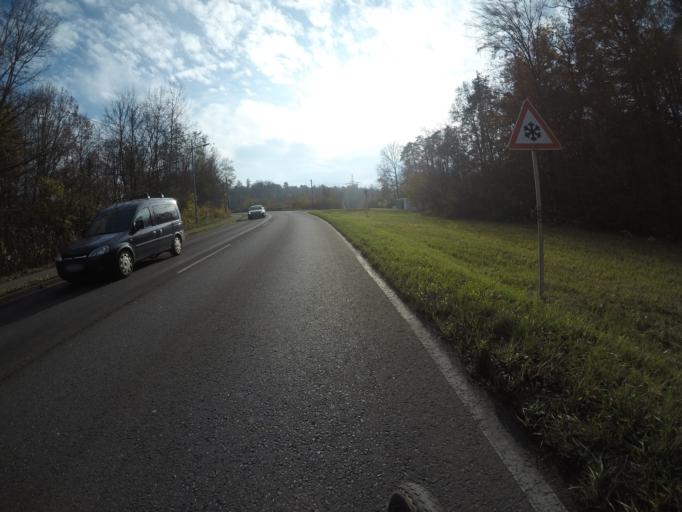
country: DE
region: Baden-Wuerttemberg
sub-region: Regierungsbezirk Stuttgart
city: Steinenbronn
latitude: 48.7122
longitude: 9.1065
